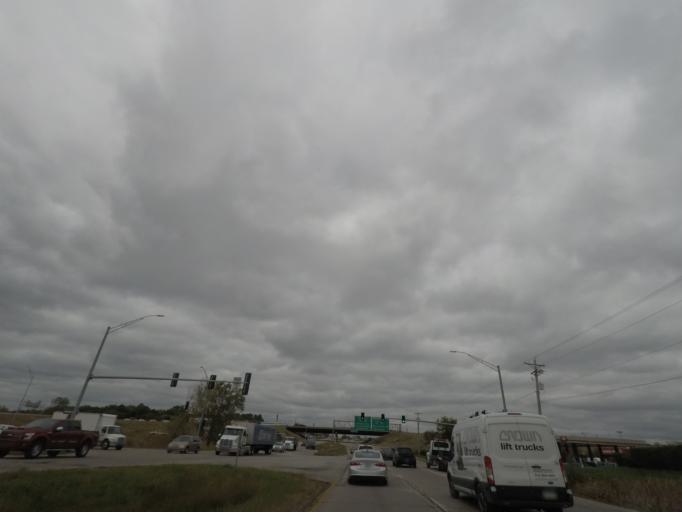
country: US
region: Iowa
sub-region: Polk County
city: Saylorville
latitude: 41.6472
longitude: -93.6004
